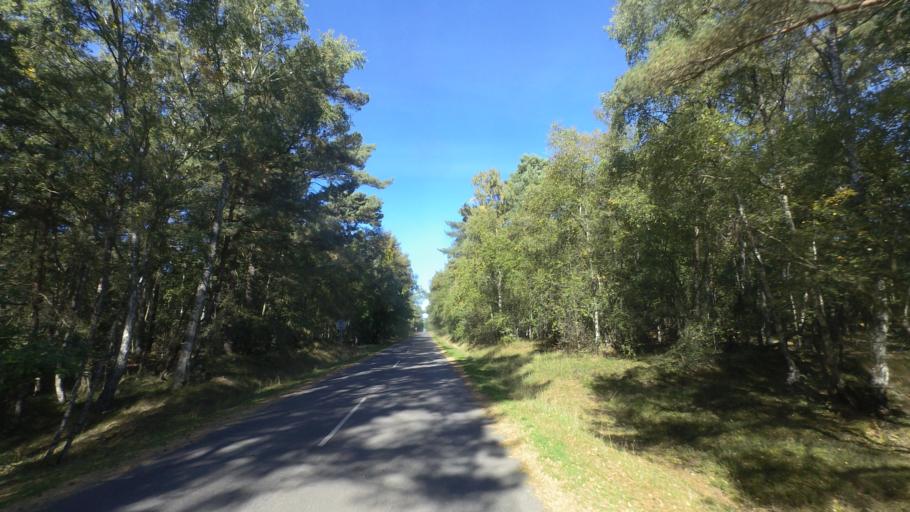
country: DK
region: Capital Region
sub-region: Bornholm Kommune
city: Nexo
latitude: 54.9970
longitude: 15.0766
